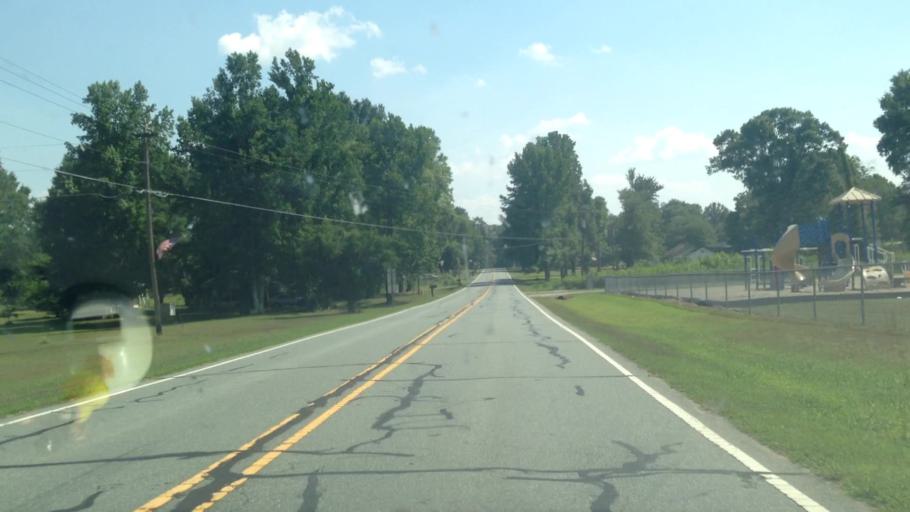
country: US
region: North Carolina
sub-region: Stokes County
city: Walnut Cove
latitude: 36.3286
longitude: -80.0479
